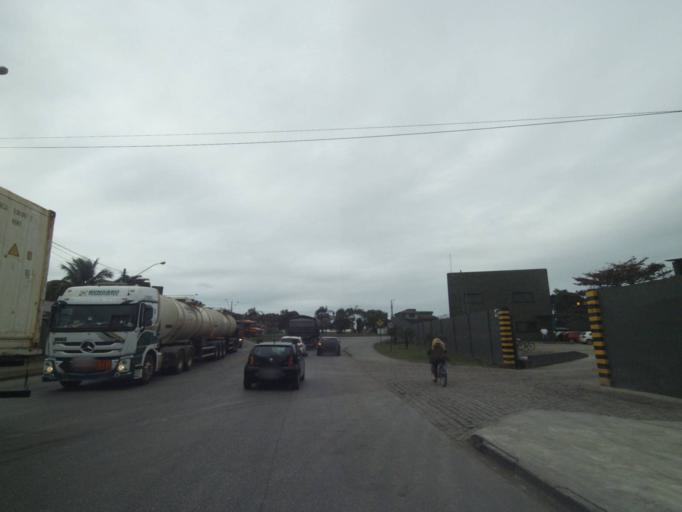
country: BR
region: Parana
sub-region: Paranagua
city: Paranagua
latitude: -25.5144
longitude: -48.5235
